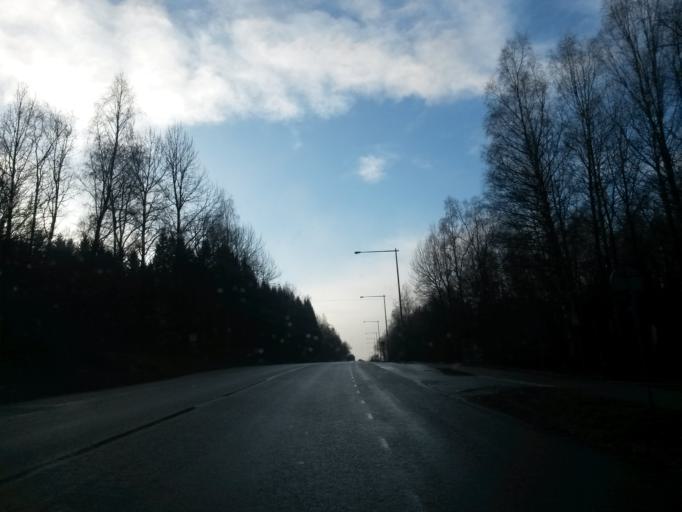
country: SE
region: Vaestra Goetaland
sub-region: Boras Kommun
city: Ganghester
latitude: 57.7893
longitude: 13.0018
